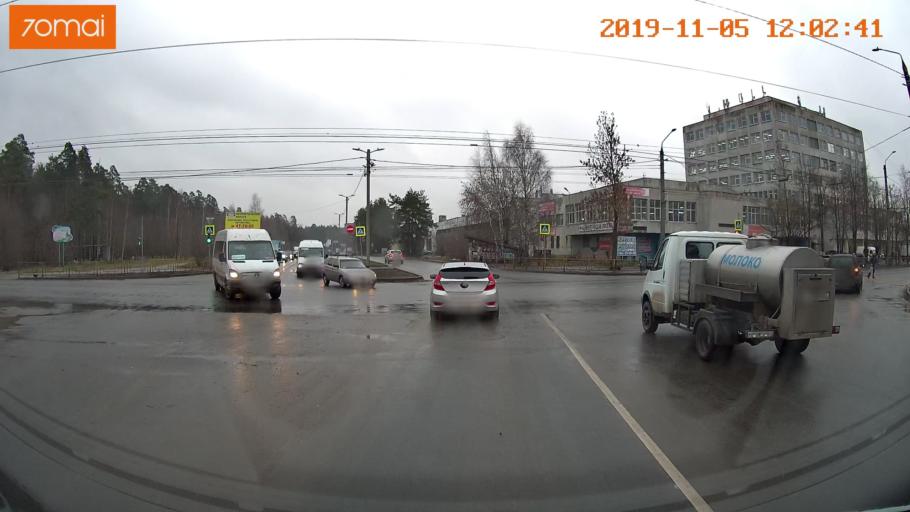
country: RU
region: Ivanovo
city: Kokhma
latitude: 56.9709
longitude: 41.0521
